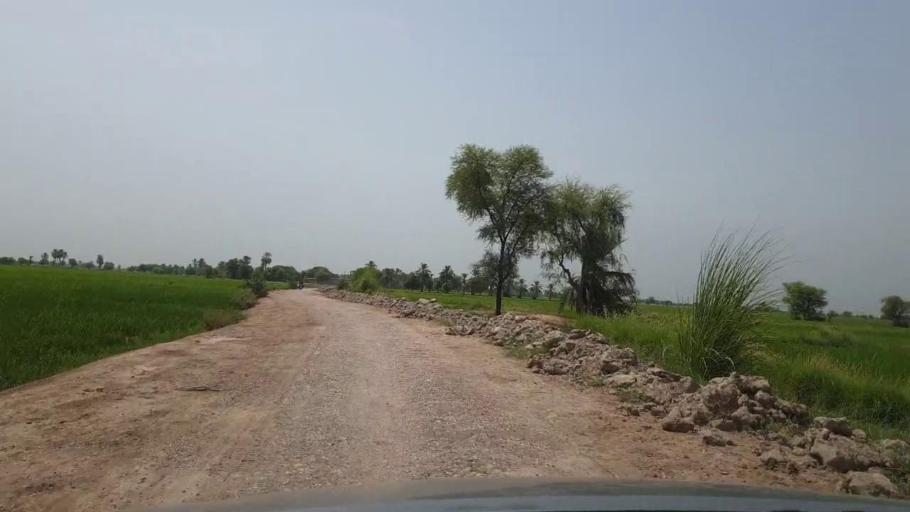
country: PK
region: Sindh
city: Madeji
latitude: 27.7910
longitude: 68.4345
